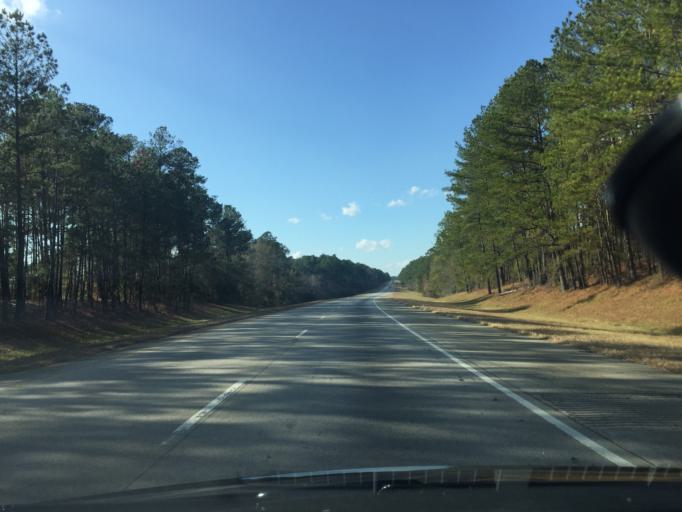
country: US
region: Georgia
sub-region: Treutlen County
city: Soperton
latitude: 32.4280
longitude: -82.4754
